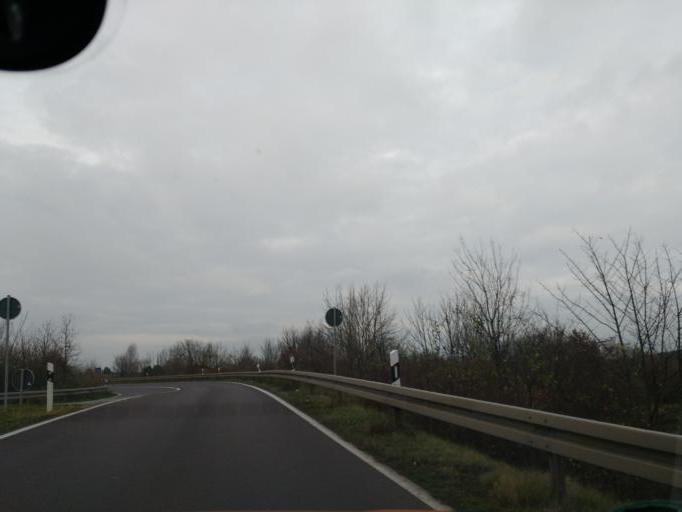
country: DE
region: Lower Saxony
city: Laatzen
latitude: 52.3603
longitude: 9.8731
